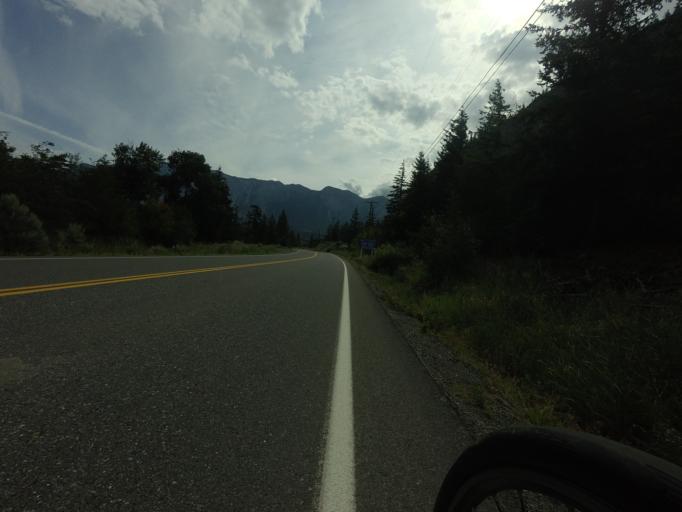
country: CA
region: British Columbia
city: Lillooet
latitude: 50.6703
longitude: -121.9559
